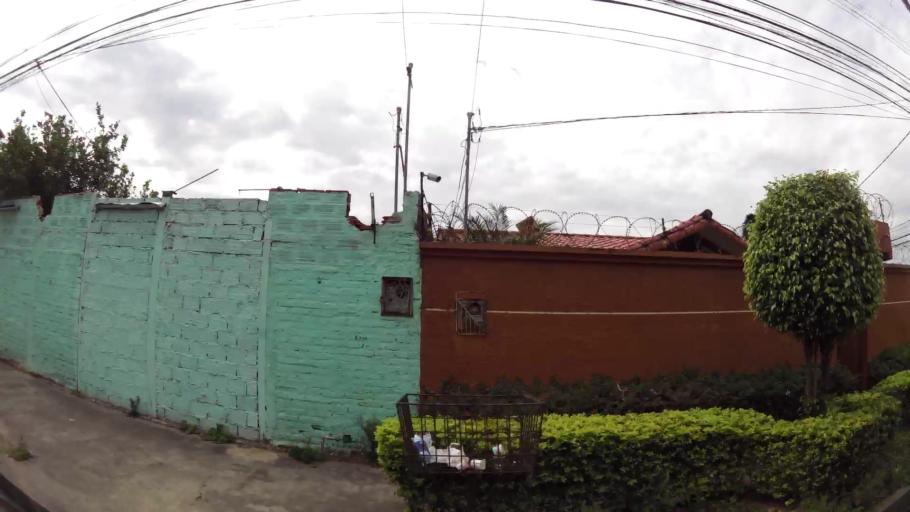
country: BO
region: Santa Cruz
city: Santa Cruz de la Sierra
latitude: -17.7459
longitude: -63.1918
